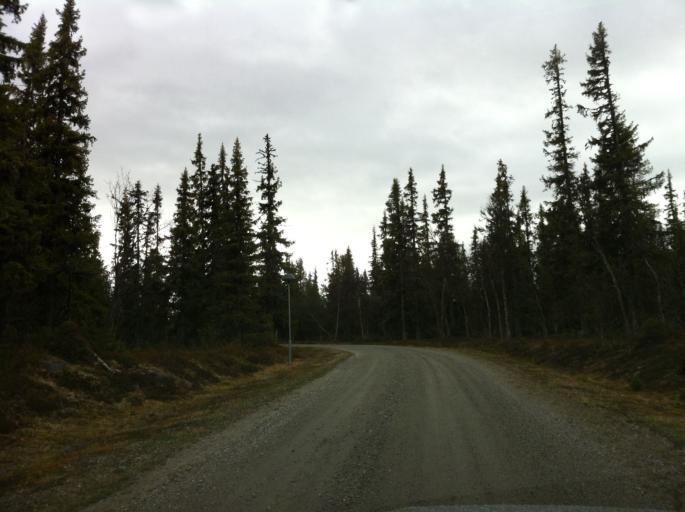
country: NO
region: Hedmark
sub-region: Engerdal
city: Engerdal
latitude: 62.5420
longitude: 12.4447
